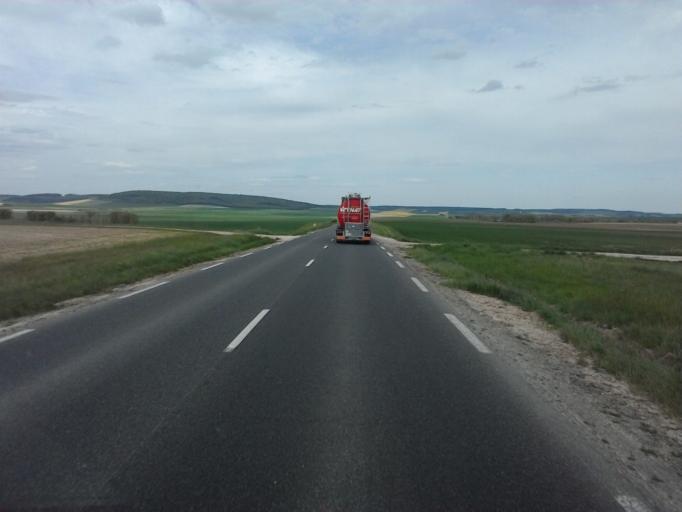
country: FR
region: Bourgogne
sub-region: Departement de l'Yonne
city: Neuvy-Sautour
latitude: 48.0504
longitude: 3.7975
